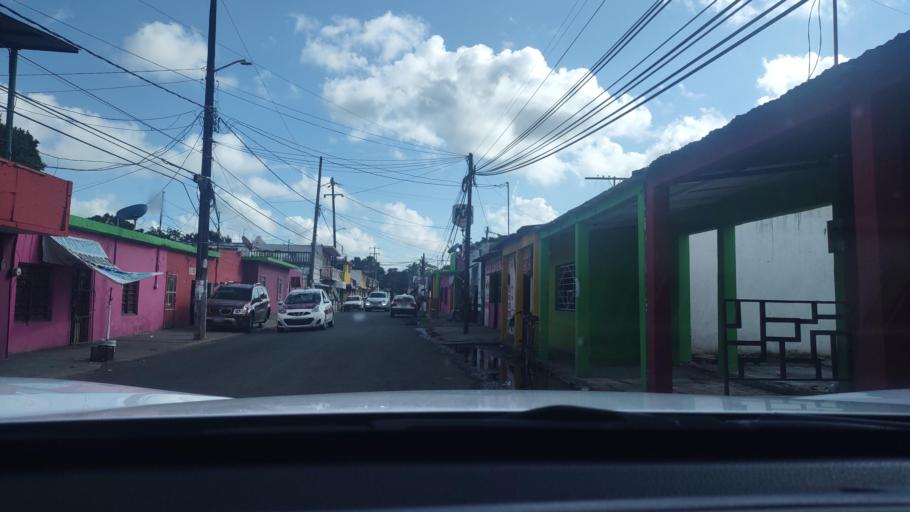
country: MX
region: Veracruz
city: El Tejar
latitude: 19.0714
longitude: -96.1616
